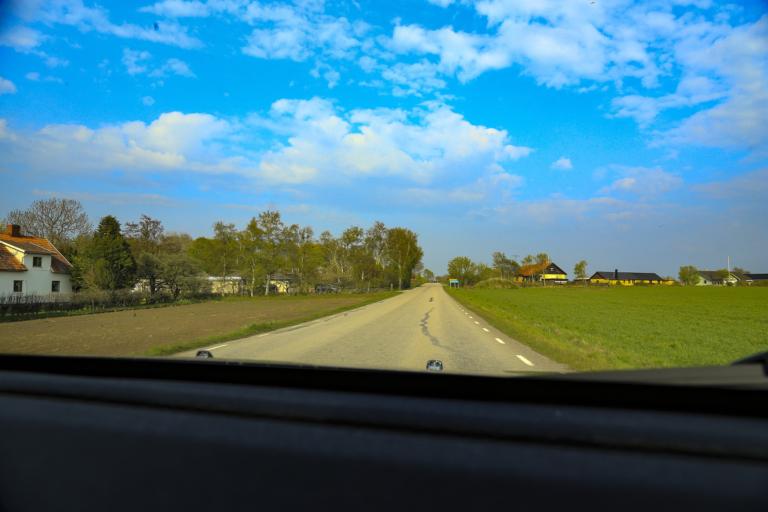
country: SE
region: Halland
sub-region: Varbergs Kommun
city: Tvaaker
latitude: 57.0995
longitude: 12.3472
